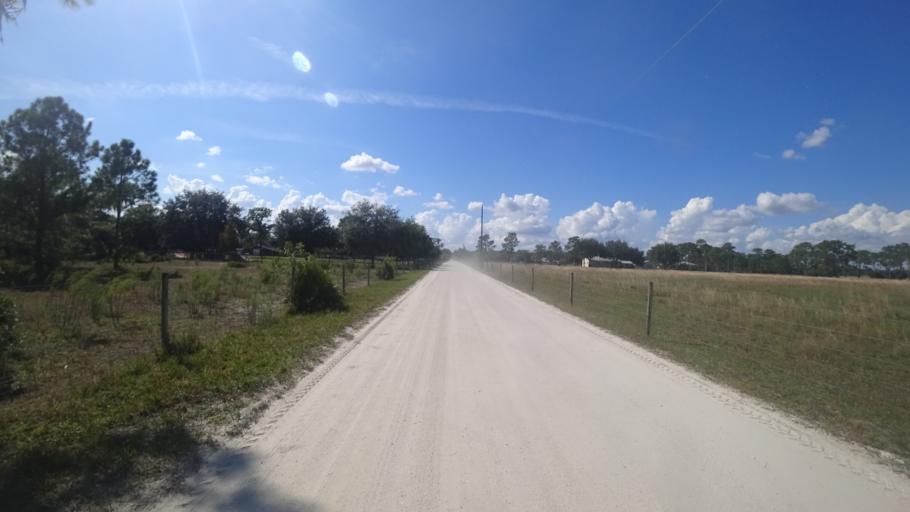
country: US
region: Florida
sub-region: Sarasota County
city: The Meadows
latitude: 27.4525
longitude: -82.2926
